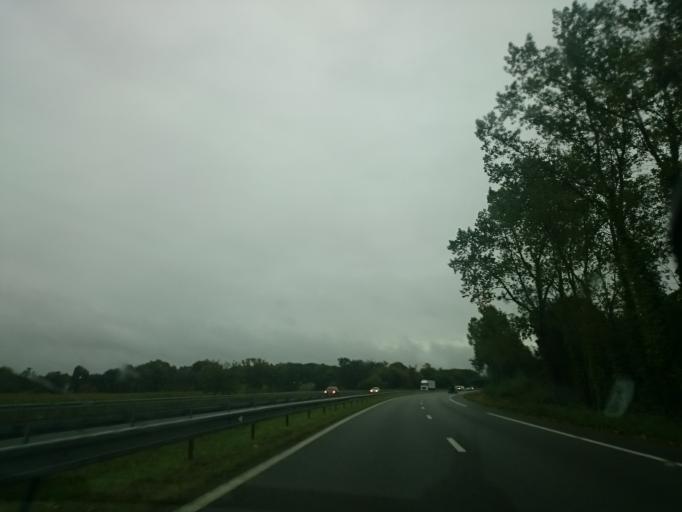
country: FR
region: Brittany
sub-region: Departement du Morbihan
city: Theix
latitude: 47.6307
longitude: -2.6415
